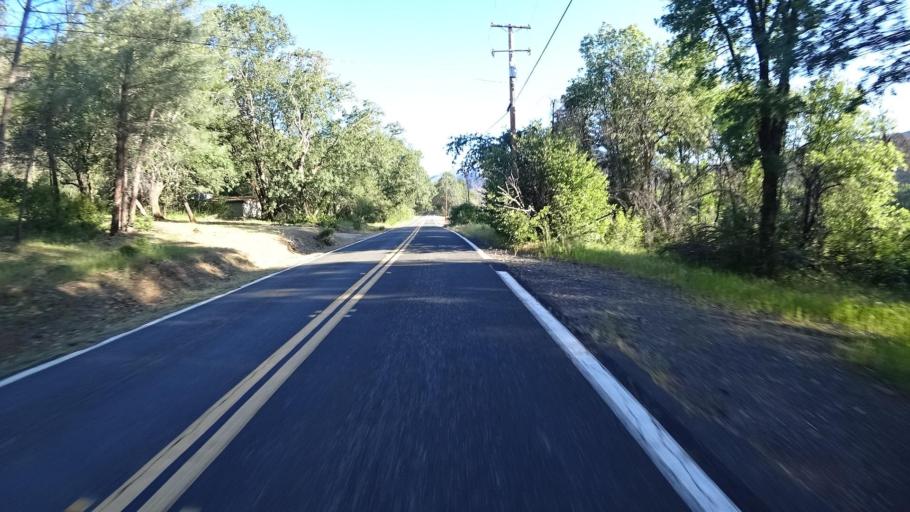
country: US
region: California
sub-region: Lake County
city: Upper Lake
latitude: 39.2297
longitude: -122.9441
